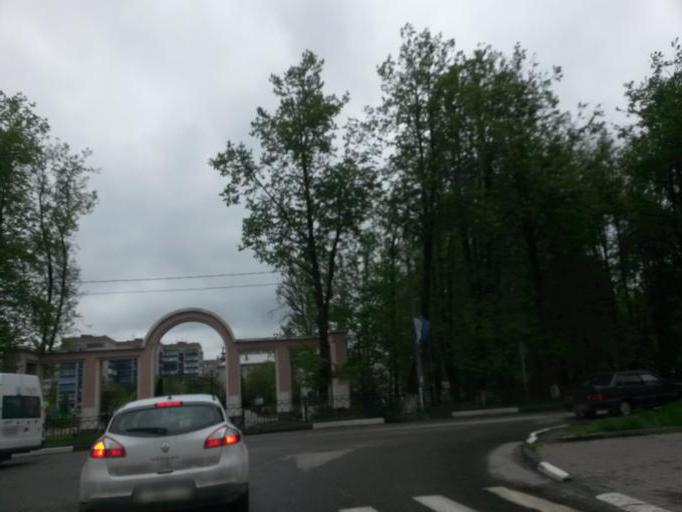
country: RU
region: Moskovskaya
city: Klimovsk
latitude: 55.3797
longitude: 37.5420
